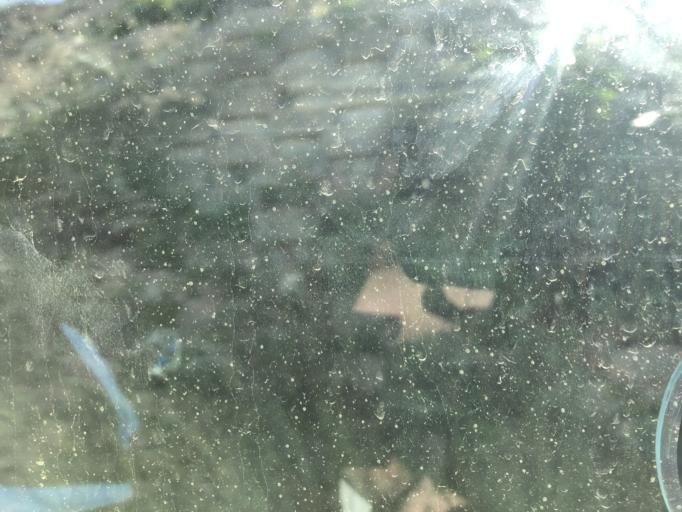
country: LS
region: Maseru
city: Maseru
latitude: -29.3228
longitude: 27.4953
